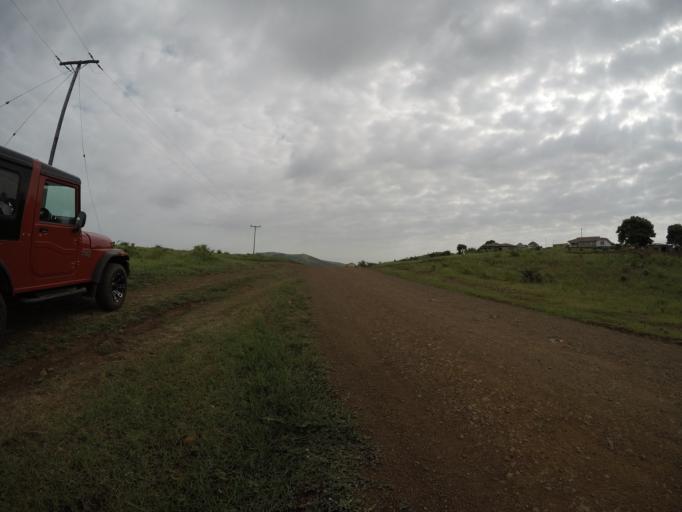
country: ZA
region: KwaZulu-Natal
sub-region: uThungulu District Municipality
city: Empangeni
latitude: -28.6370
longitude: 31.9045
